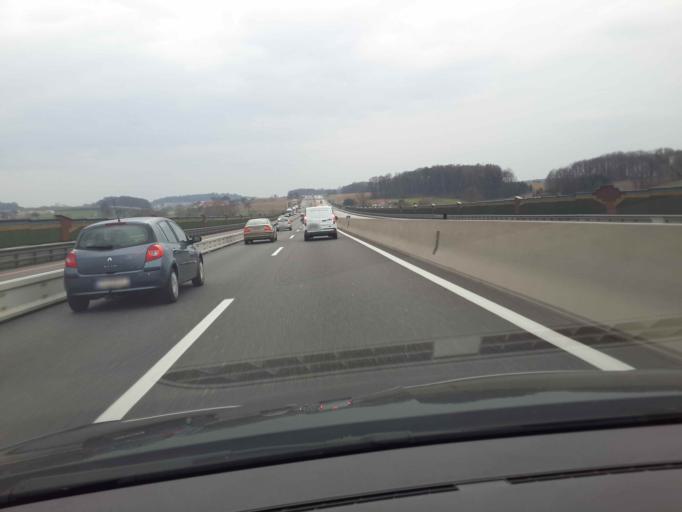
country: AT
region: Lower Austria
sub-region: Politischer Bezirk Sankt Polten
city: Boheimkirchen
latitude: 48.1864
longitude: 15.7323
